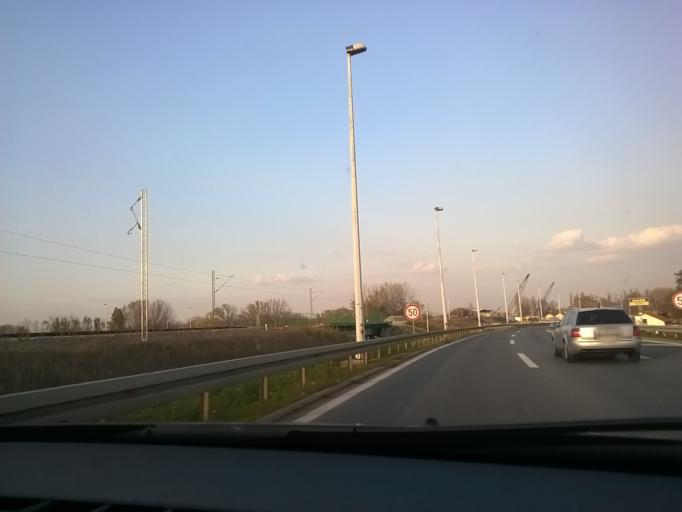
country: RS
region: Central Serbia
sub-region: Belgrade
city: Palilula
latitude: 44.8367
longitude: 20.4942
